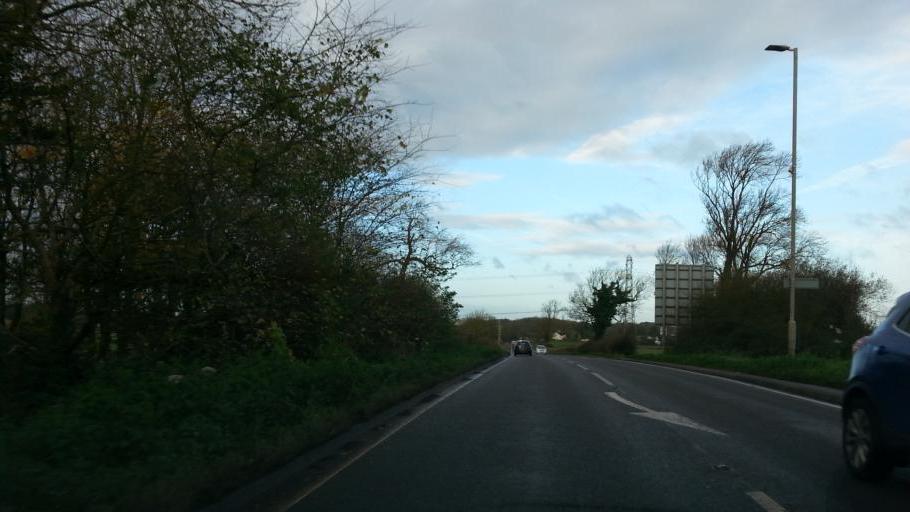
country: GB
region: England
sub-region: Leicestershire
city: Coalville
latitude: 52.7316
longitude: -1.3962
